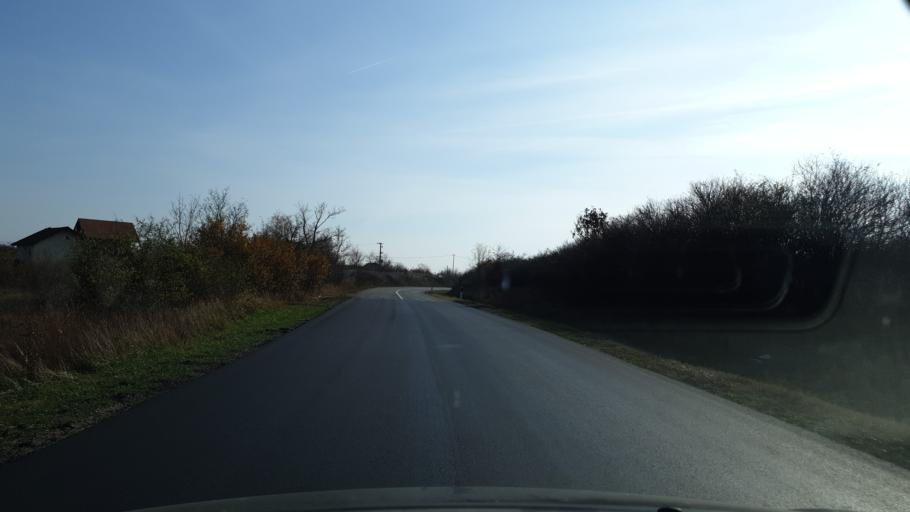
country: RS
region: Central Serbia
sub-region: Borski Okrug
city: Bor
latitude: 44.0213
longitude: 22.0703
